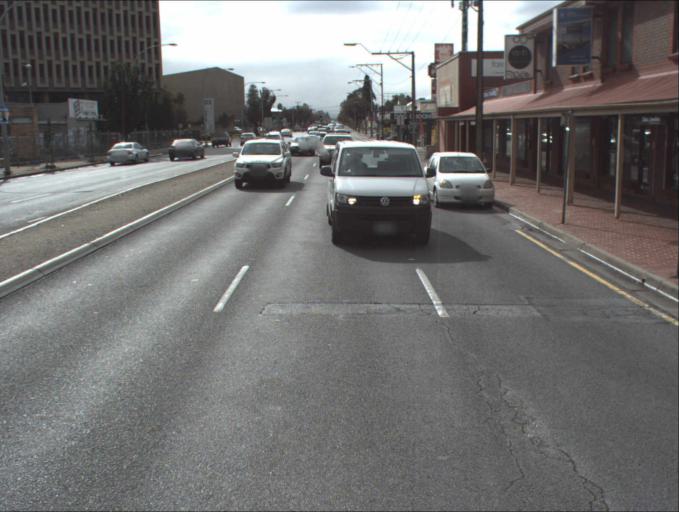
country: AU
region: South Australia
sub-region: Prospect
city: Prospect
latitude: -34.8893
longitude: 138.6134
